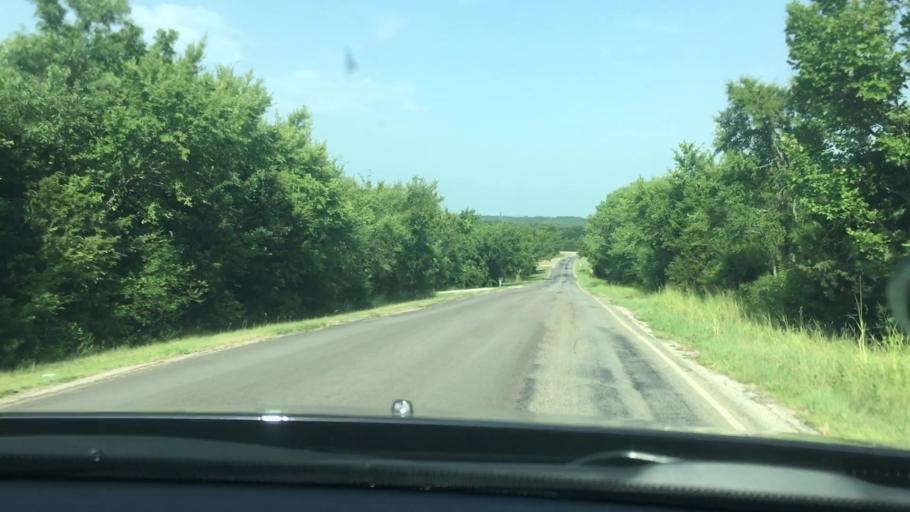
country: US
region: Oklahoma
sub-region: Pontotoc County
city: Byng
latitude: 34.8648
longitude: -96.6173
